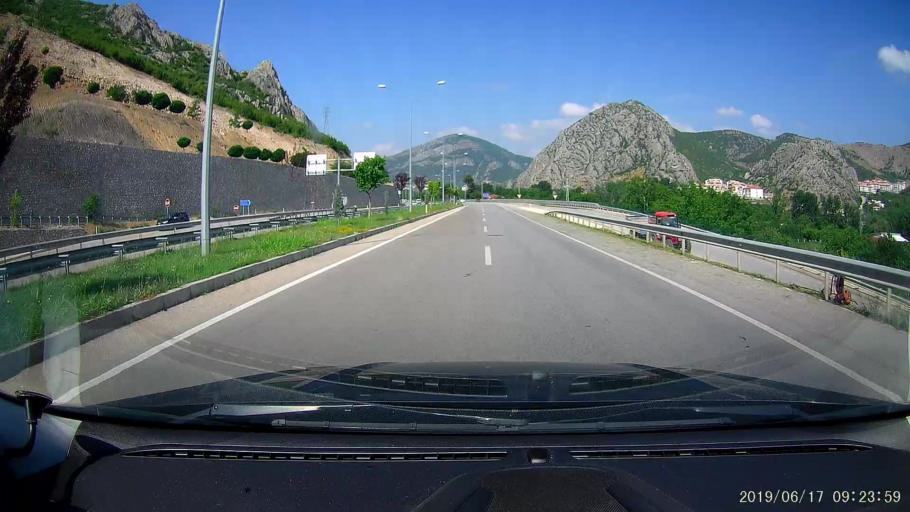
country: TR
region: Amasya
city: Amasya
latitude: 40.6741
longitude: 35.8638
